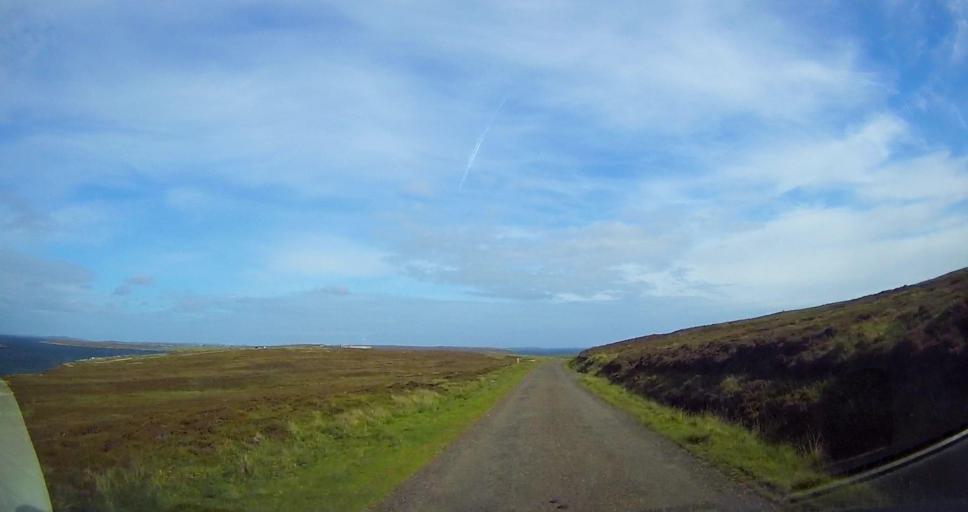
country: GB
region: Scotland
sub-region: Orkney Islands
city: Stromness
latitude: 58.8564
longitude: -3.2137
